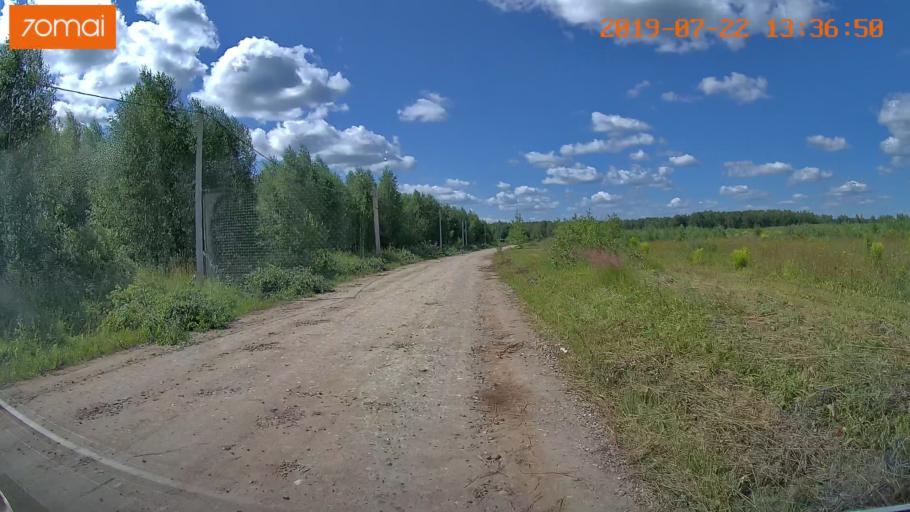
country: RU
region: Ivanovo
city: Novo-Talitsy
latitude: 57.0668
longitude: 40.8891
